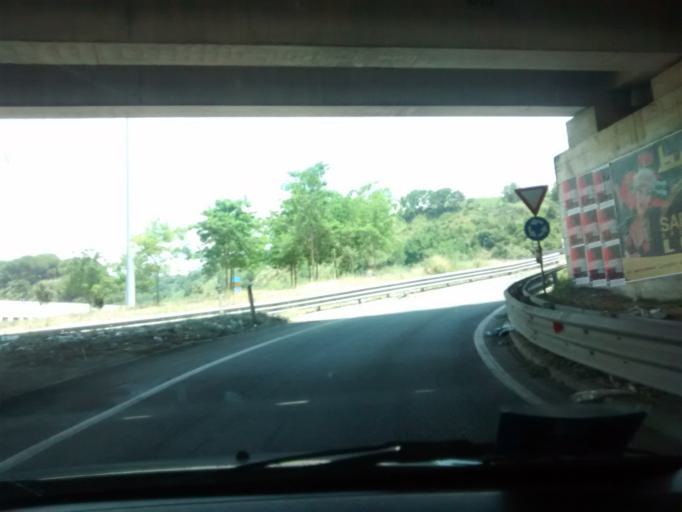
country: IT
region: Calabria
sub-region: Provincia di Catanzaro
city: Pianopoli
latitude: 38.9032
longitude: 16.3847
